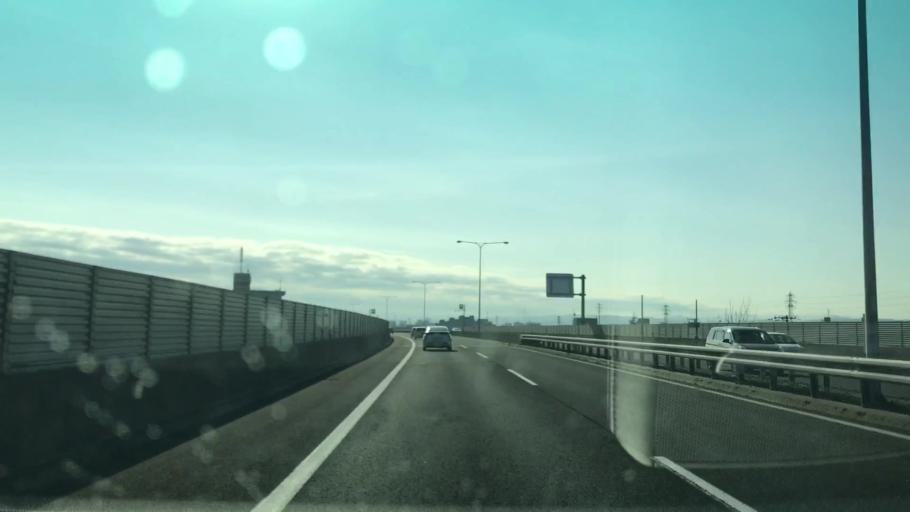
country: JP
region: Hokkaido
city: Sapporo
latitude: 43.0620
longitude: 141.4245
